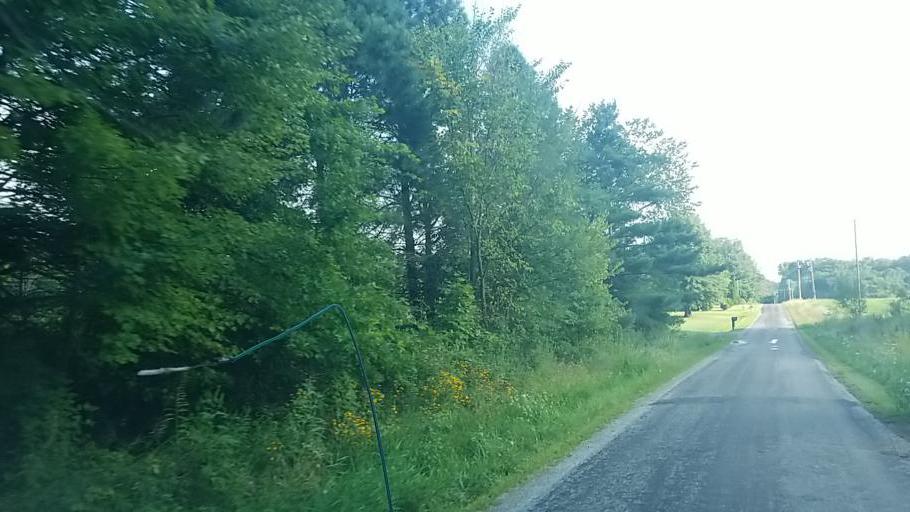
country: US
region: Ohio
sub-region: Wayne County
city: West Salem
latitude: 40.8771
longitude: -82.1926
